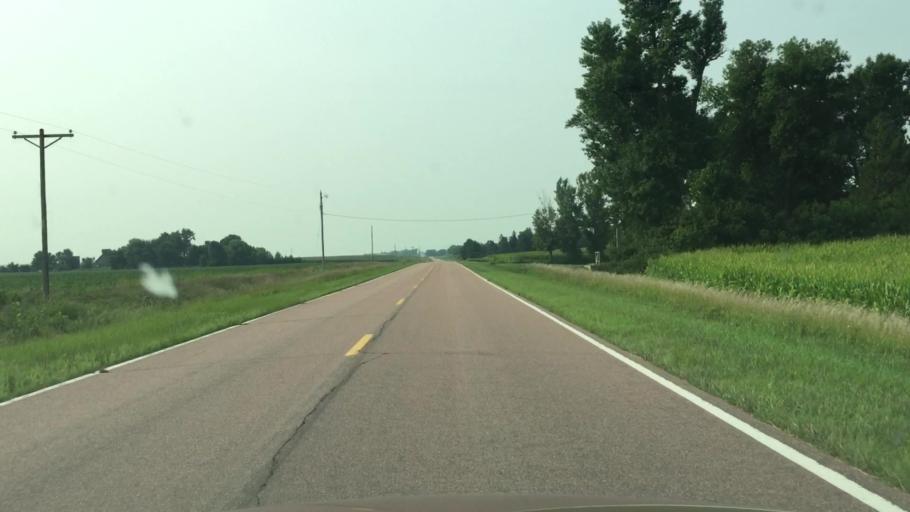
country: US
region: Iowa
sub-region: O'Brien County
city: Sheldon
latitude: 43.2496
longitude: -95.7833
